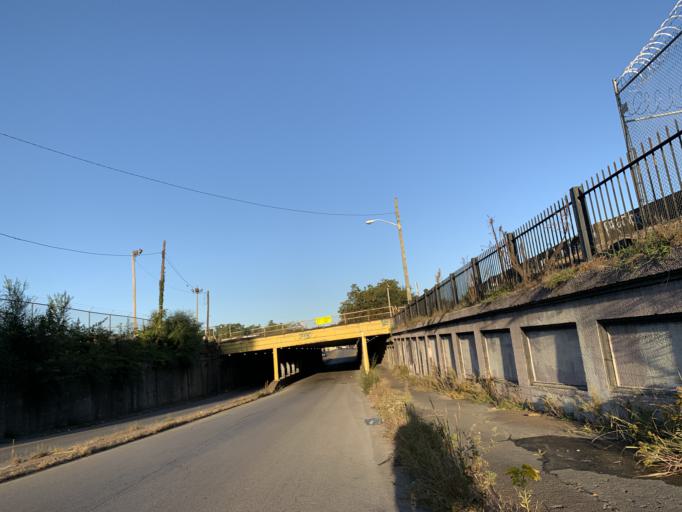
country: US
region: Kentucky
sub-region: Jefferson County
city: Louisville
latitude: 38.2365
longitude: -85.7757
